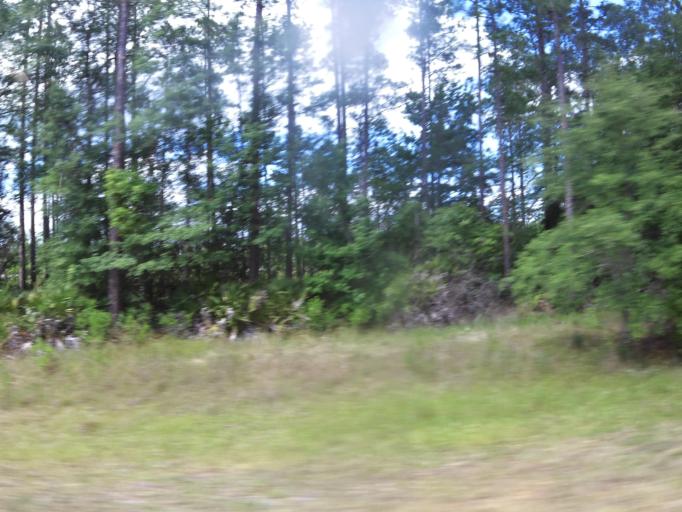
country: US
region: Florida
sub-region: Clay County
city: Asbury Lake
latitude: 29.9117
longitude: -81.8863
